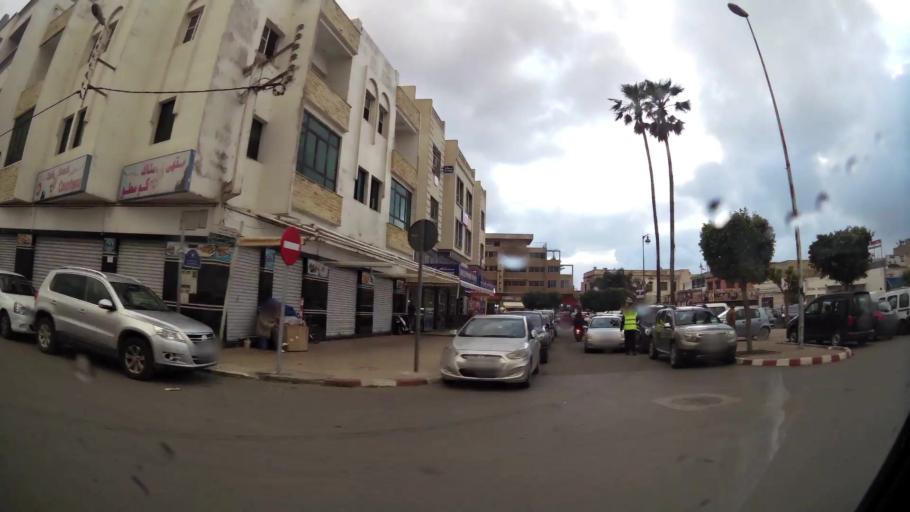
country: MA
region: Doukkala-Abda
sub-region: El-Jadida
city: El Jadida
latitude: 33.2549
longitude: -8.5033
